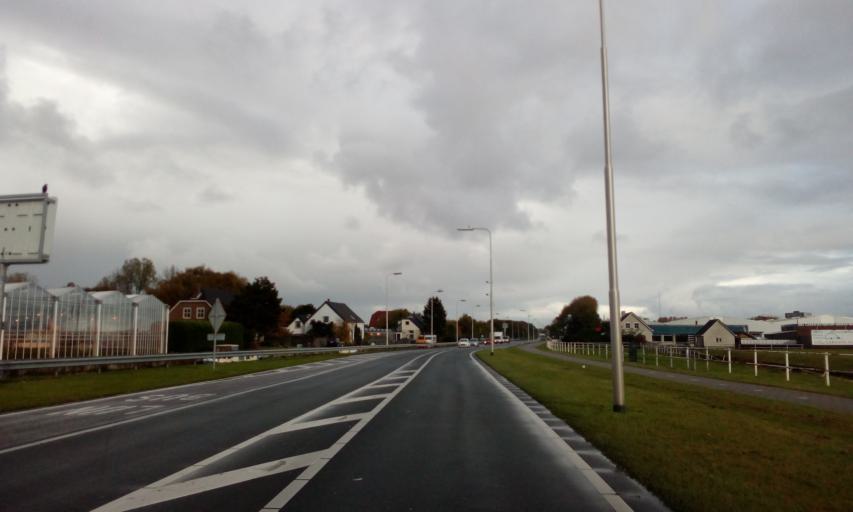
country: NL
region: South Holland
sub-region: Gemeente Westland
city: Poeldijk
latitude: 52.0329
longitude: 4.2263
